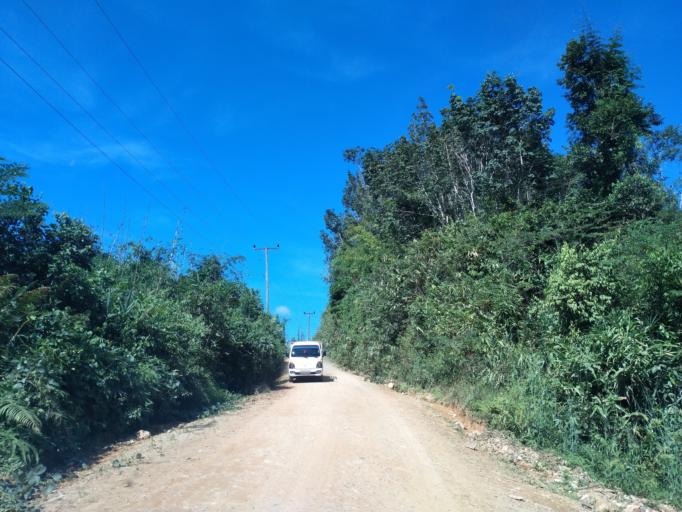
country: TH
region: Changwat Bueng Kan
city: Pak Khat
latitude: 18.6294
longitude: 103.0722
